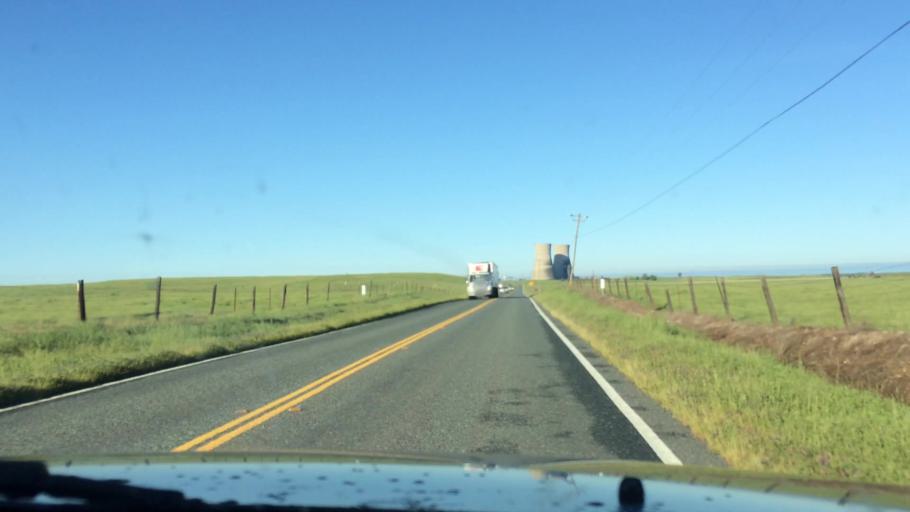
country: US
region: California
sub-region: Sacramento County
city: Clay
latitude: 38.3574
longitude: -121.0921
